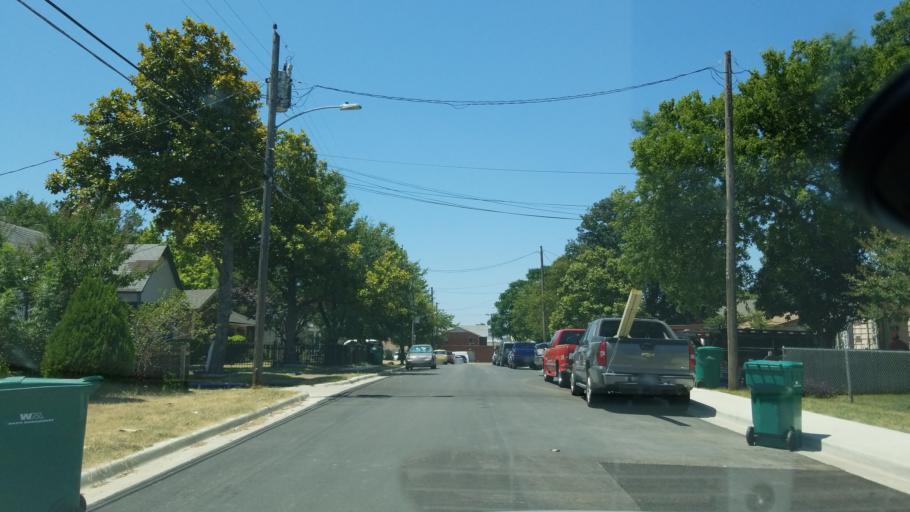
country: US
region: Texas
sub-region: Dallas County
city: Cockrell Hill
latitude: 32.7375
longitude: -96.8859
